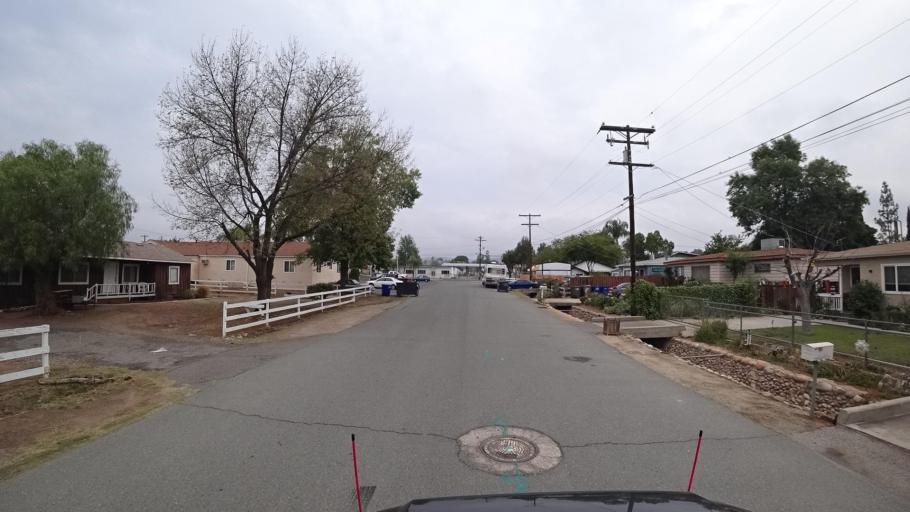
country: US
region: California
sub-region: San Diego County
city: Ramona
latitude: 33.0406
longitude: -116.8665
